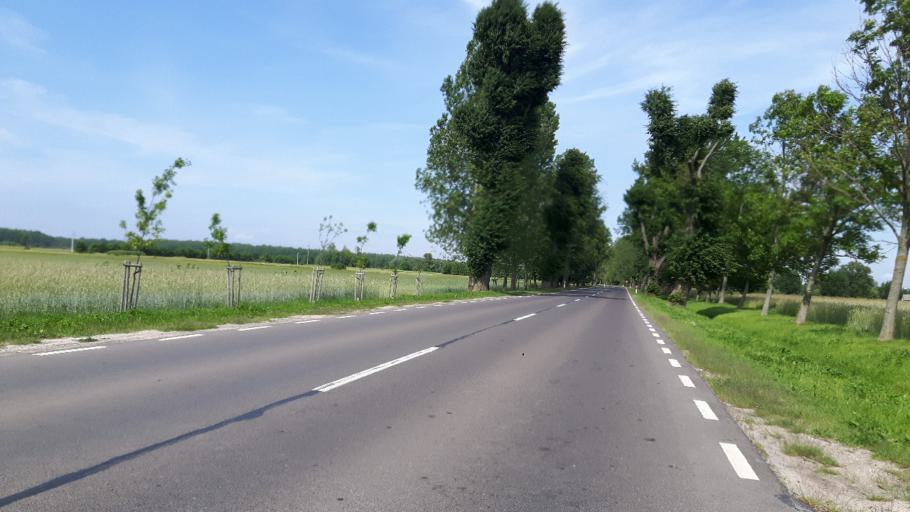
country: RU
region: Kaliningrad
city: Mamonovo
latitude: 54.4242
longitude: 19.8846
